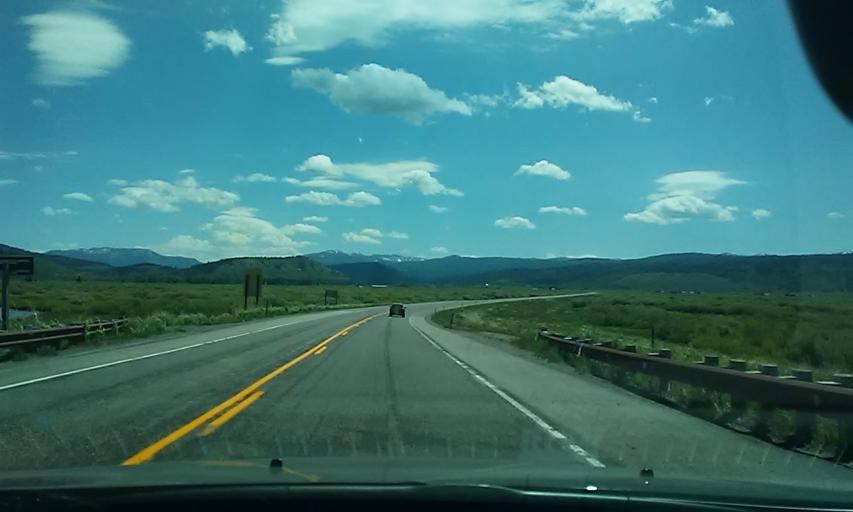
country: US
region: Wyoming
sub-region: Teton County
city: Jackson
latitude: 43.8381
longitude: -110.4399
